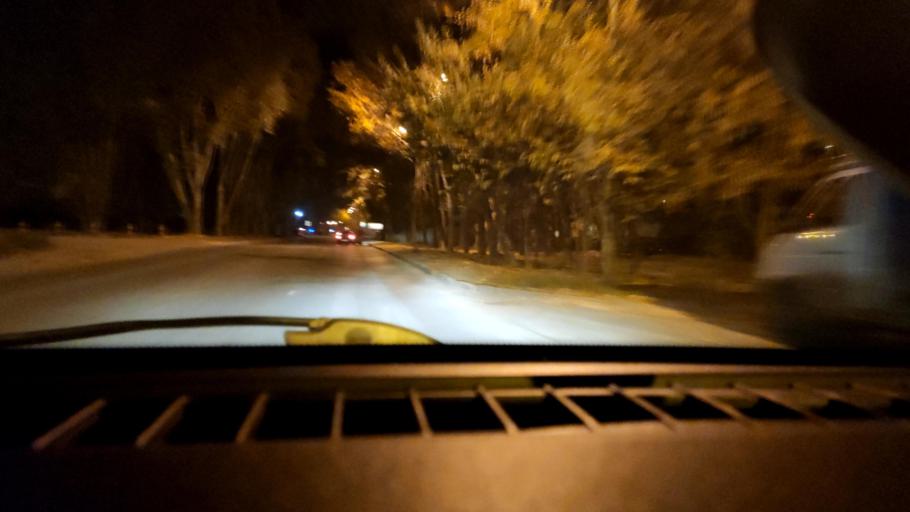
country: RU
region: Samara
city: Petra-Dubrava
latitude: 53.2305
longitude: 50.2918
